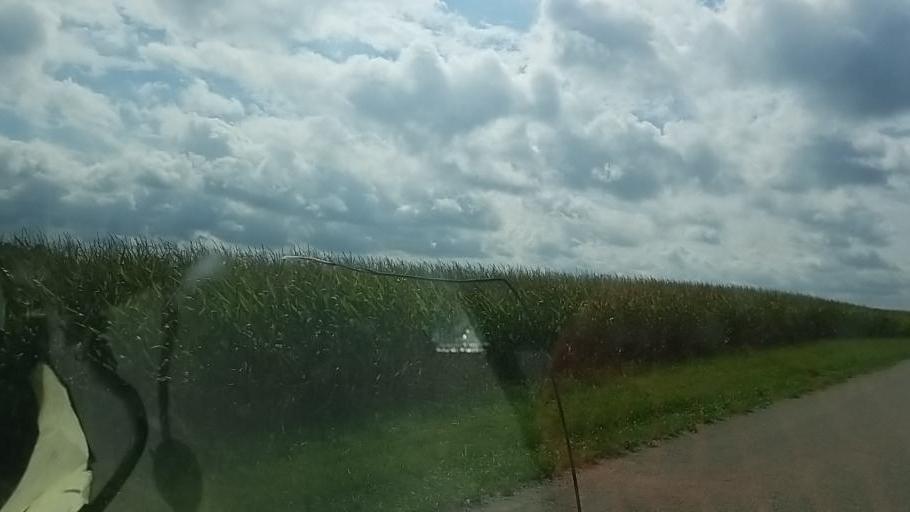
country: US
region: Ohio
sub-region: Pickaway County
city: Commercial Point
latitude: 39.7915
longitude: -83.1004
